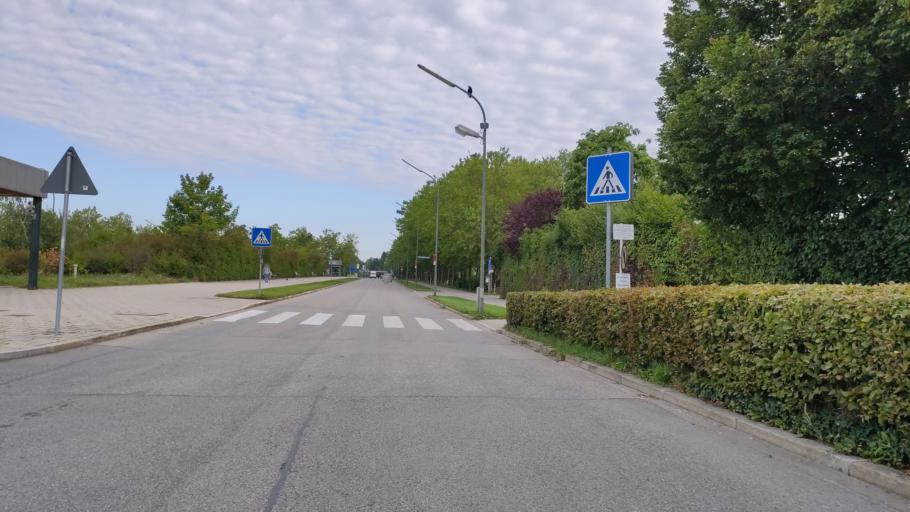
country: DE
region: Bavaria
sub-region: Upper Bavaria
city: Neuried
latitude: 48.1095
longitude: 11.4743
